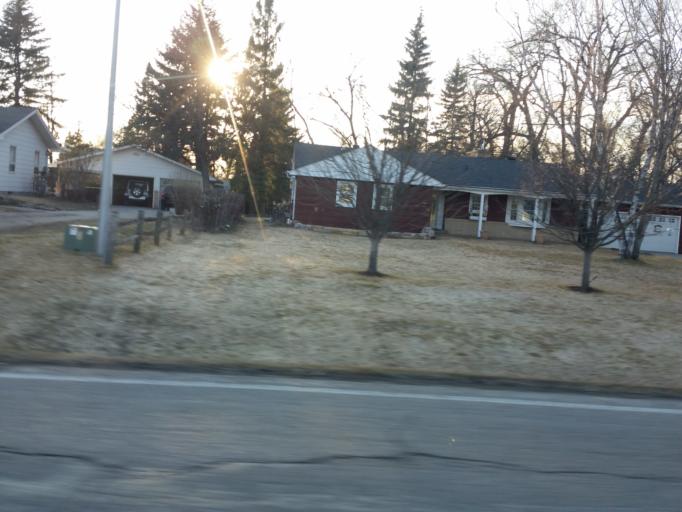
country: US
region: North Dakota
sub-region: Grand Forks County
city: Grand Forks
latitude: 47.8733
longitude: -97.0292
